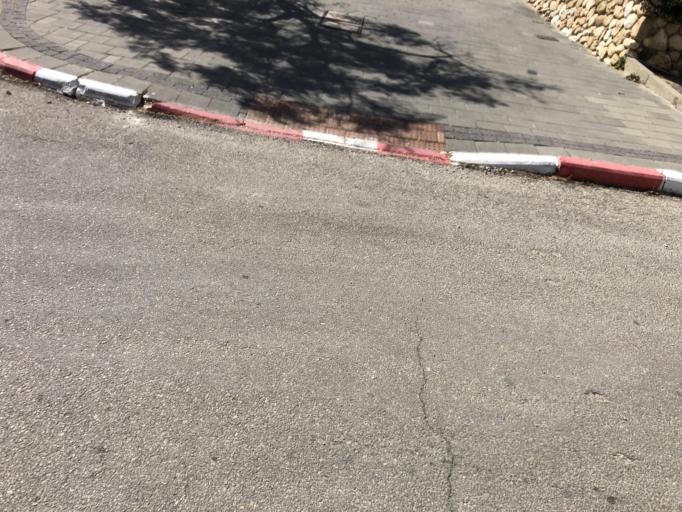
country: IL
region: Tel Aviv
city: Bat Yam
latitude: 32.0090
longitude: 34.7585
